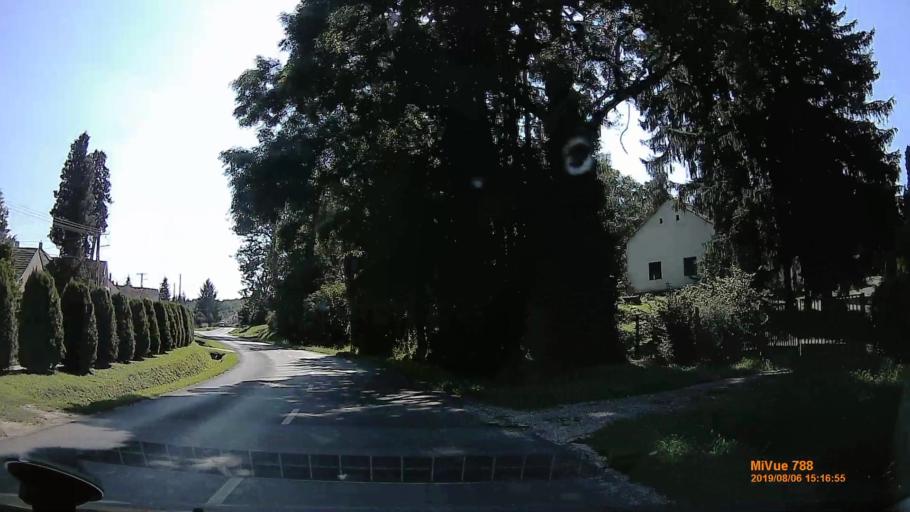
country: HU
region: Zala
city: Murakeresztur
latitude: 46.3185
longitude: 16.9678
